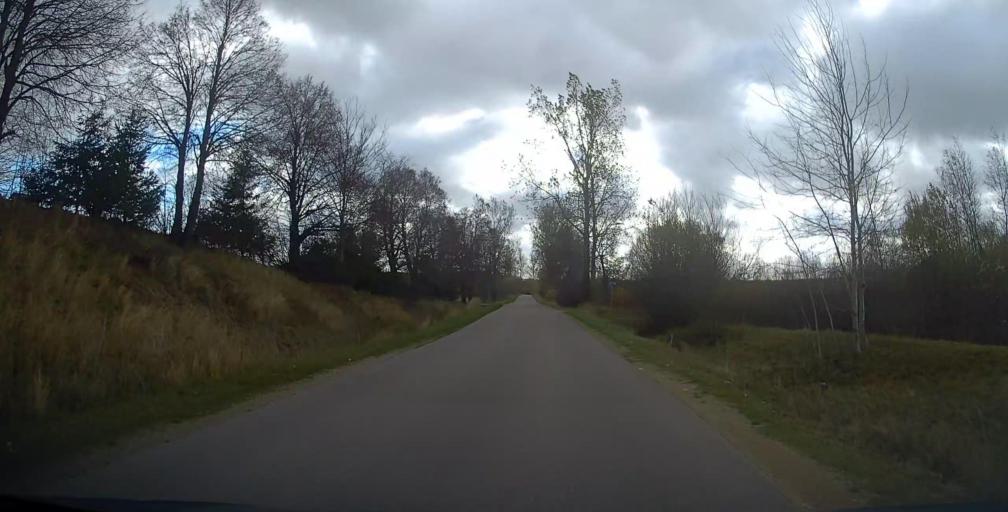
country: PL
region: Podlasie
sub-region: Suwalki
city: Suwalki
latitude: 54.3552
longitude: 22.8552
